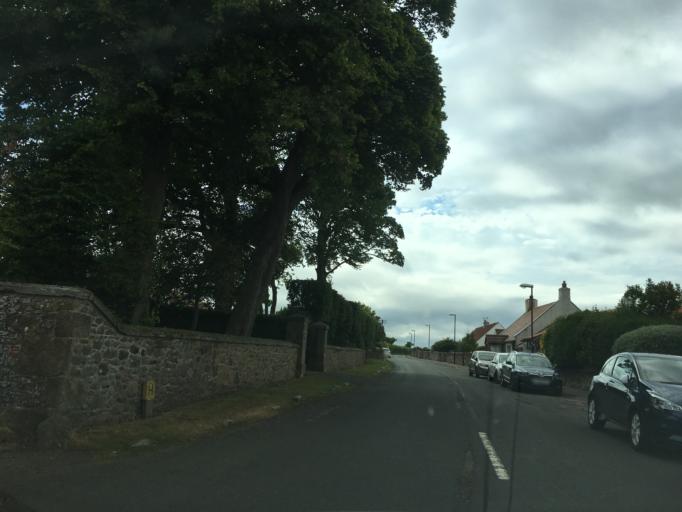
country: GB
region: Scotland
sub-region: East Lothian
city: Haddington
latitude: 55.9864
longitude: -2.7499
